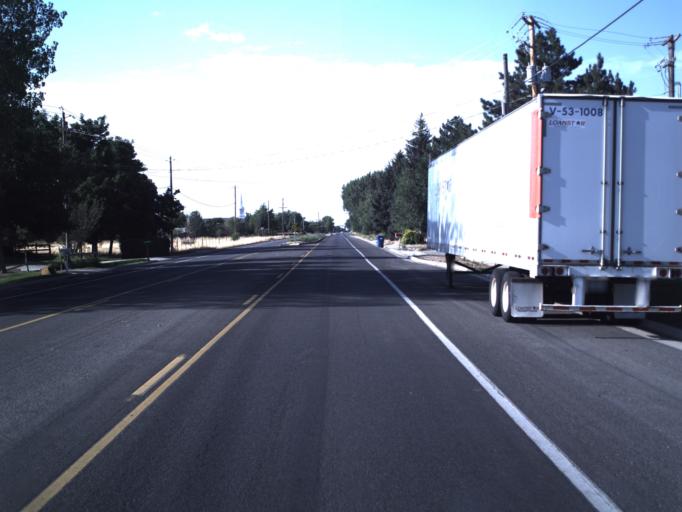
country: US
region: Utah
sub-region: Utah County
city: Alpine
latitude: 40.4385
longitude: -111.7846
